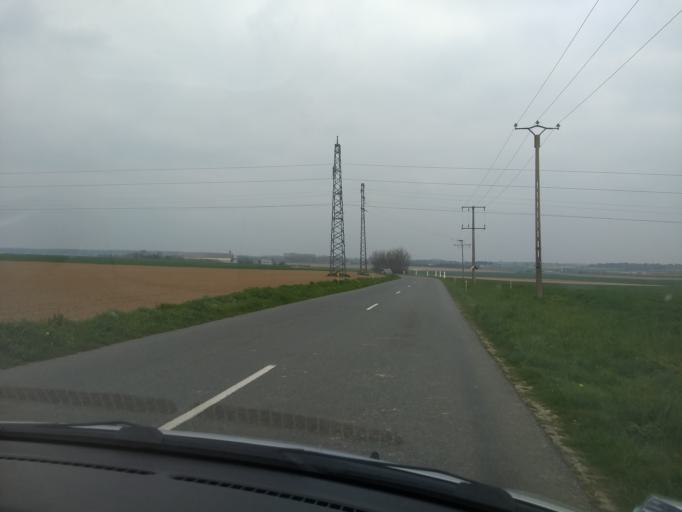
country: FR
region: Nord-Pas-de-Calais
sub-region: Departement du Pas-de-Calais
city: Maroeuil
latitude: 50.3509
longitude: 2.7257
